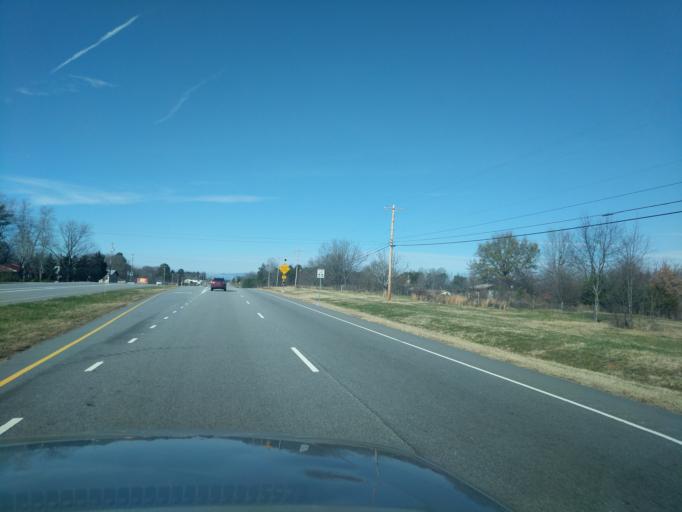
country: US
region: North Carolina
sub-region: Rutherford County
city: Forest City
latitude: 35.2867
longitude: -81.9034
